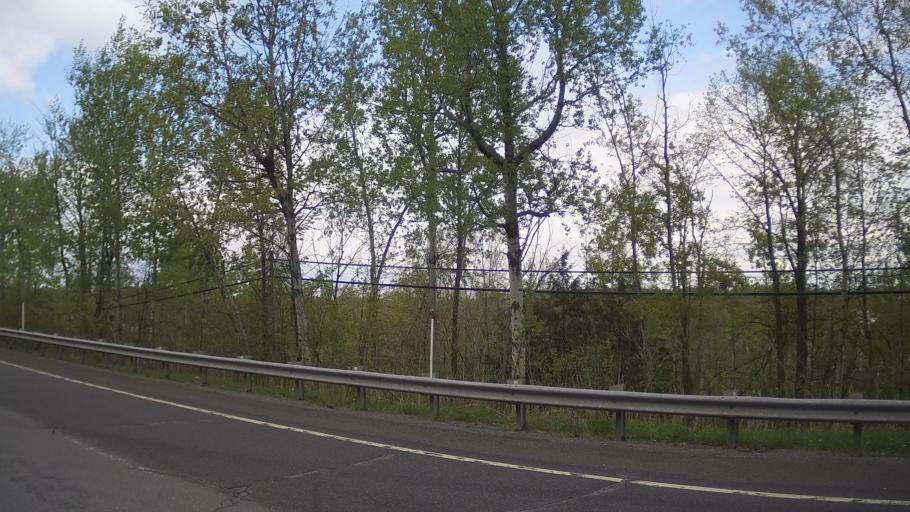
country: CA
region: Quebec
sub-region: Monteregie
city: Cowansville
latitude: 45.1990
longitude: -72.7160
